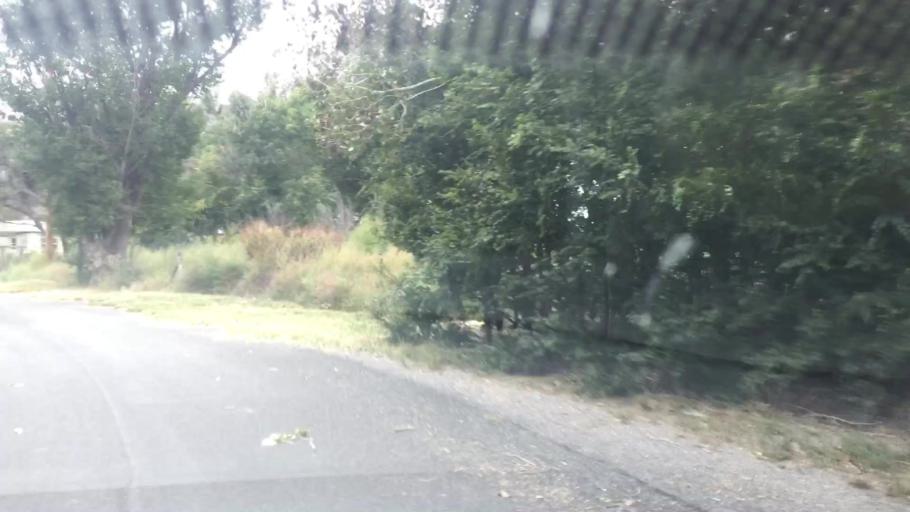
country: US
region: Kansas
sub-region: Hamilton County
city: Syracuse
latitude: 38.0577
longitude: -102.1122
